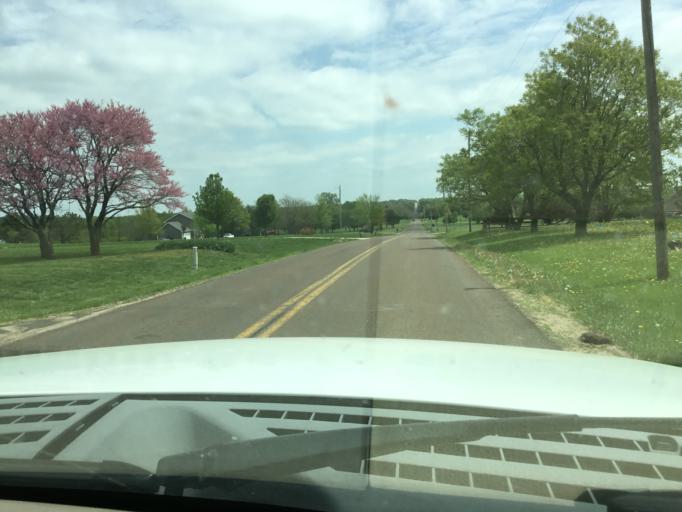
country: US
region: Kansas
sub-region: Shawnee County
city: Auburn
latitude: 38.9707
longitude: -95.7961
